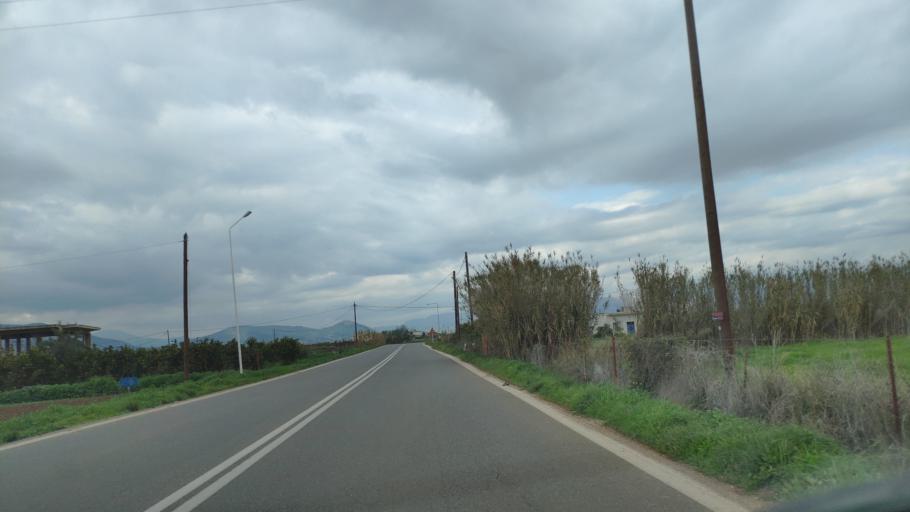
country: GR
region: Peloponnese
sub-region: Nomos Argolidos
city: Nea Kios
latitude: 37.5629
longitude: 22.7095
